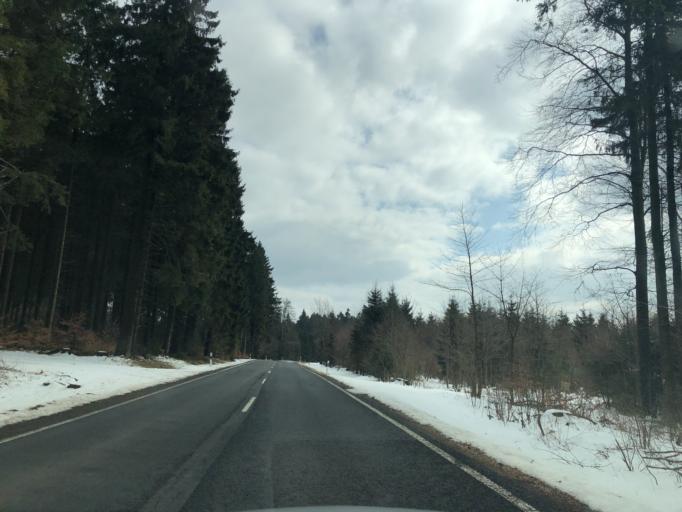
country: DE
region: Hesse
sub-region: Regierungsbezirk Giessen
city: Ulrichstein
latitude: 50.5316
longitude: 9.2255
